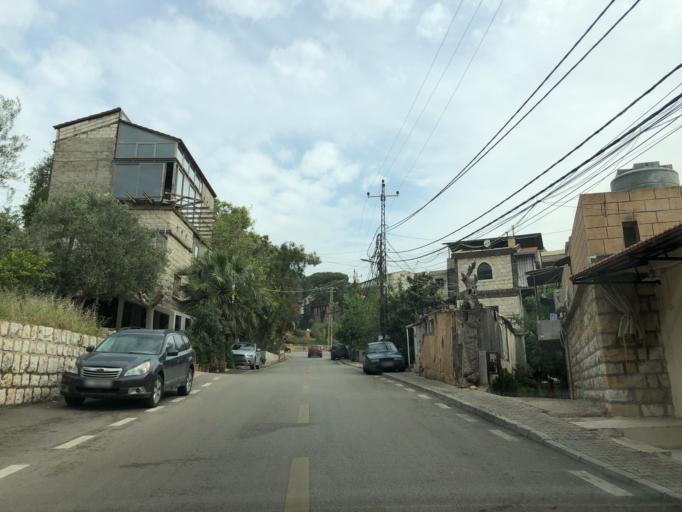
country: LB
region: Mont-Liban
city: Jdaidet el Matn
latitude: 33.8651
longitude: 35.6056
